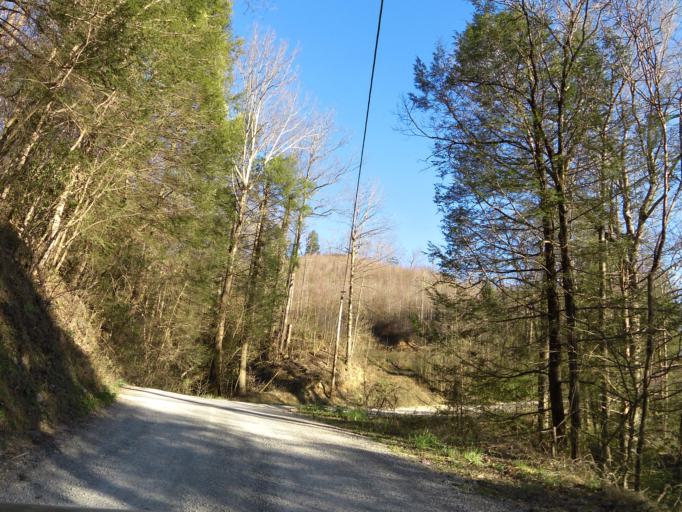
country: US
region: Tennessee
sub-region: Campbell County
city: Caryville
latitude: 36.2612
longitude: -84.3516
